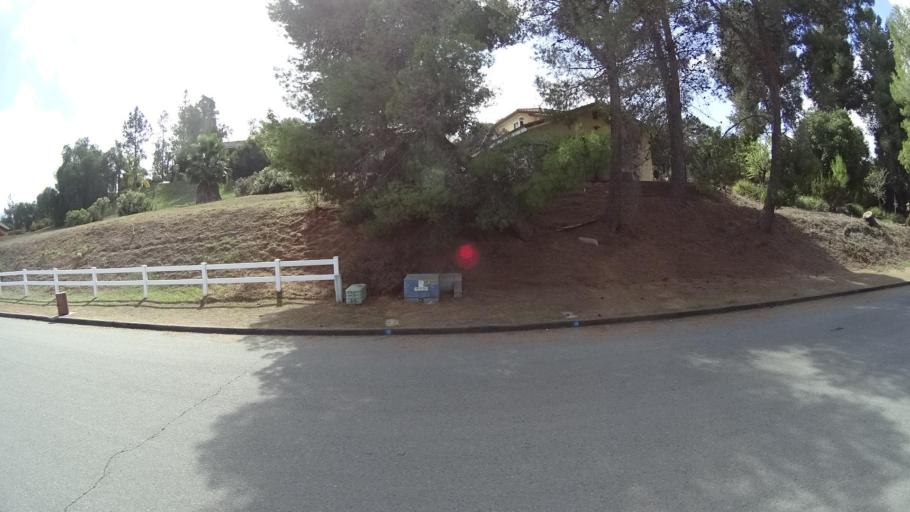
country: US
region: California
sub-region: San Diego County
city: Granite Hills
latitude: 32.7795
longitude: -116.8982
